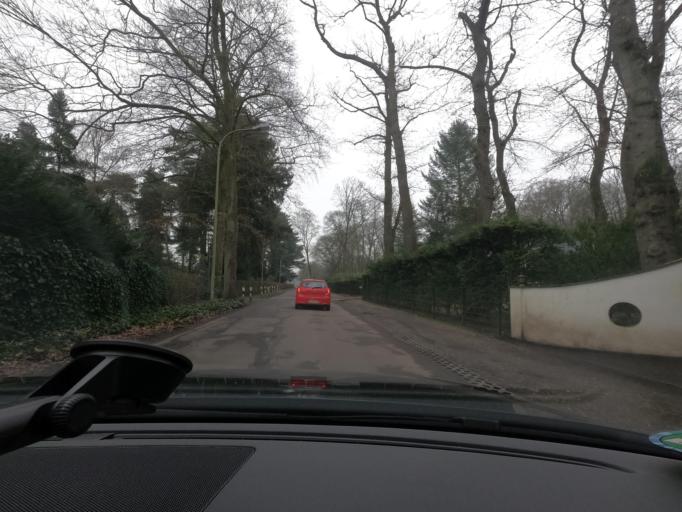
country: DE
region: North Rhine-Westphalia
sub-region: Regierungsbezirk Dusseldorf
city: Krefeld
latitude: 51.3958
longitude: 6.5358
